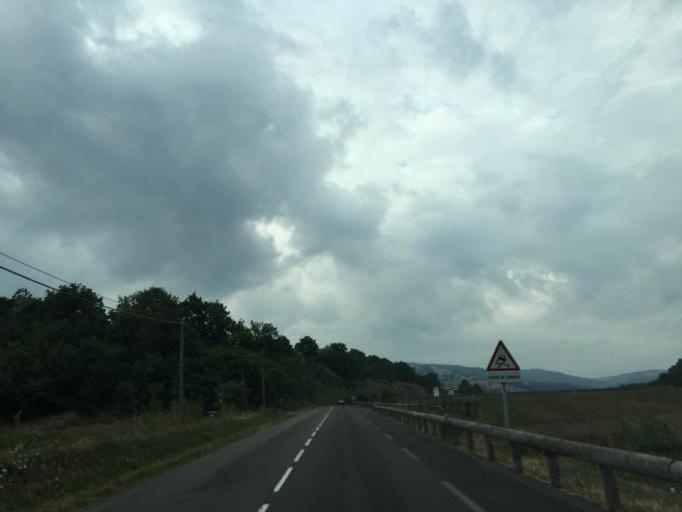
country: FR
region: Rhone-Alpes
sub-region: Departement de la Loire
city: Sorbiers
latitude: 45.5085
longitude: 4.4393
